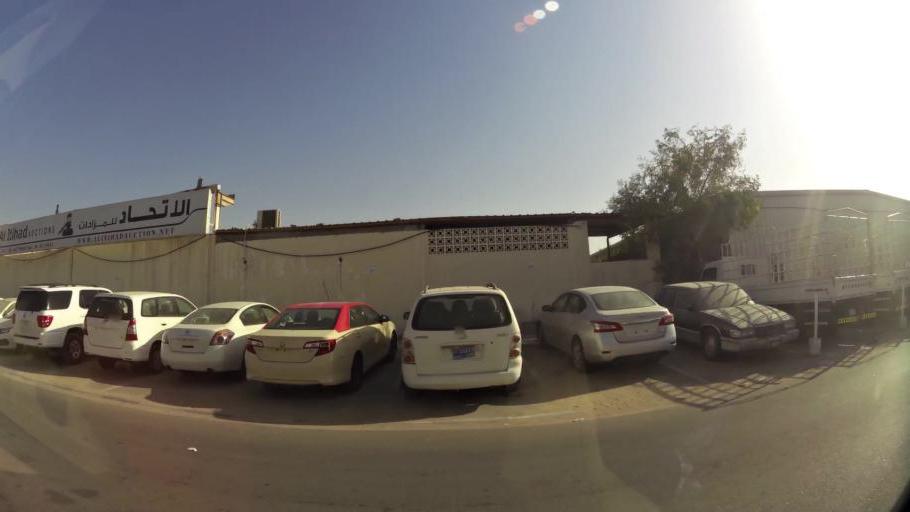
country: AE
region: Ash Shariqah
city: Sharjah
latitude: 25.2903
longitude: 55.3906
